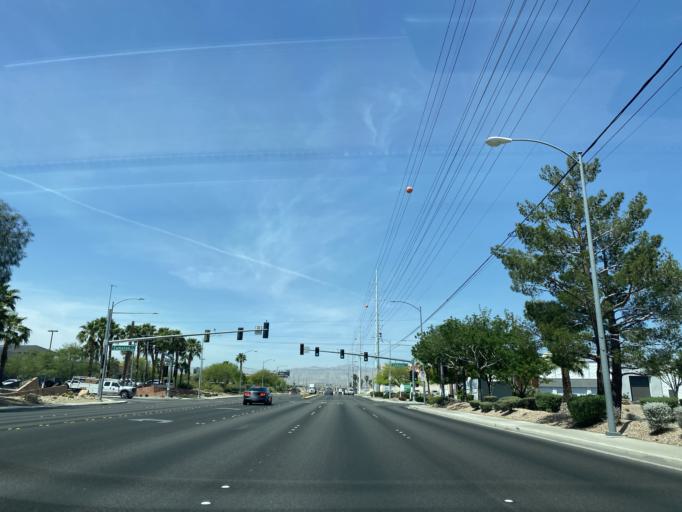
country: US
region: Nevada
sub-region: Clark County
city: Spring Valley
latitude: 36.0864
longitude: -115.2029
